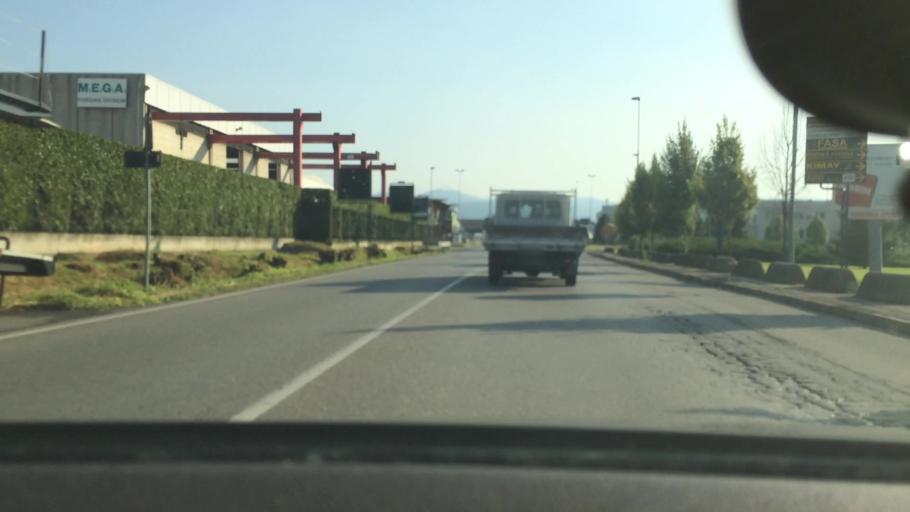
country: IT
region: Lombardy
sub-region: Provincia di Bergamo
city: Lallio
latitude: 45.6550
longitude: 9.6245
